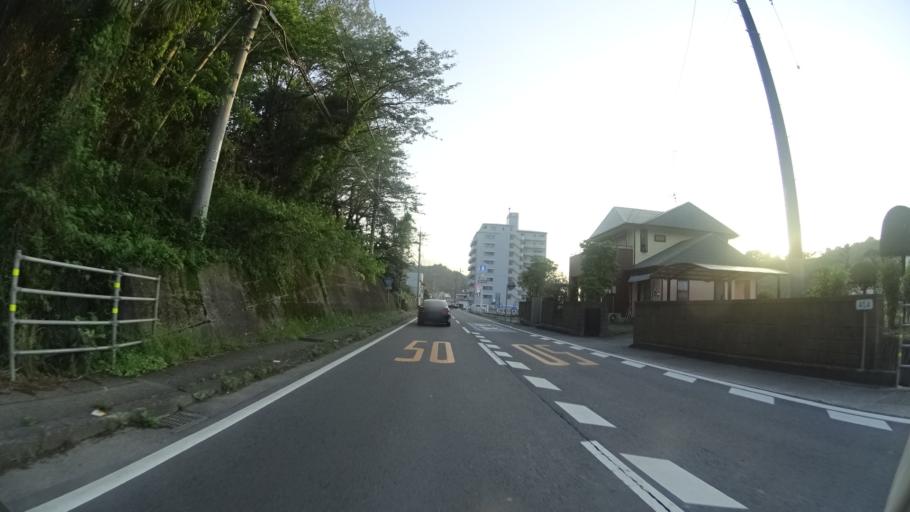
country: JP
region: Ehime
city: Kawanoecho
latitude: 33.9924
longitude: 133.6004
